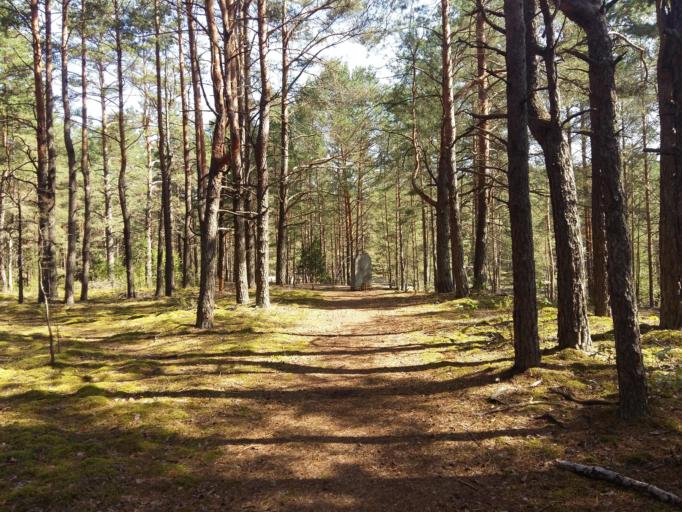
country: LT
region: Alytaus apskritis
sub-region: Alytaus rajonas
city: Daugai
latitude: 54.1587
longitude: 24.1931
